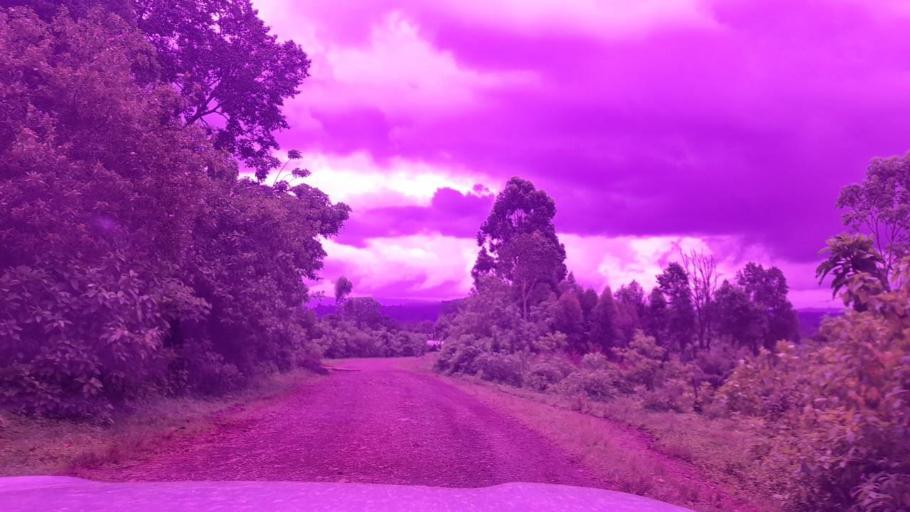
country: ET
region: Southern Nations, Nationalities, and People's Region
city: Tippi
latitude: 7.6321
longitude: 35.5784
